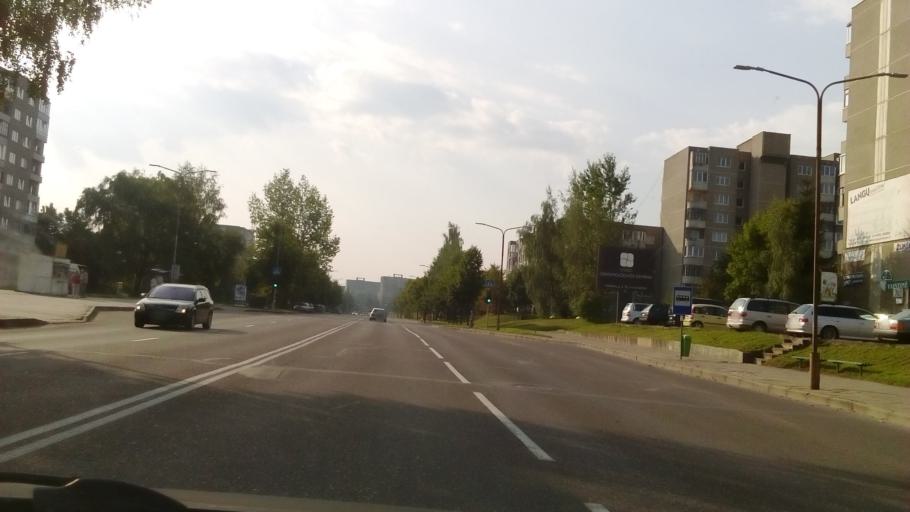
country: LT
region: Alytaus apskritis
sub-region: Alytus
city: Alytus
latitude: 54.3975
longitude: 24.0157
